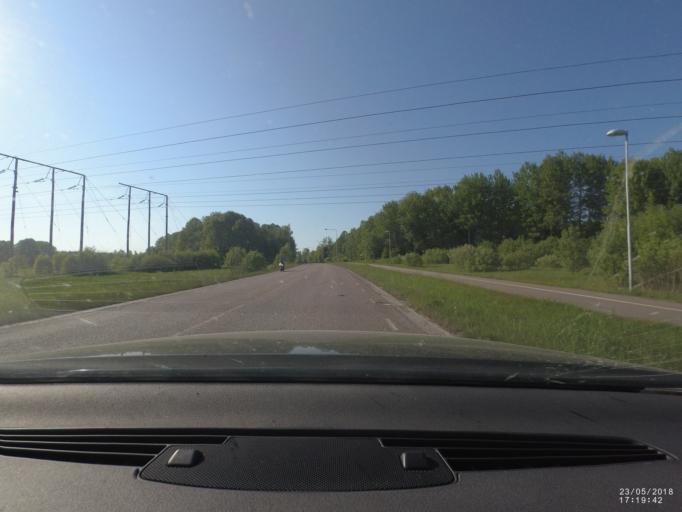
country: SE
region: Soedermanland
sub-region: Nykopings Kommun
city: Nykoping
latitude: 58.7237
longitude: 17.0207
